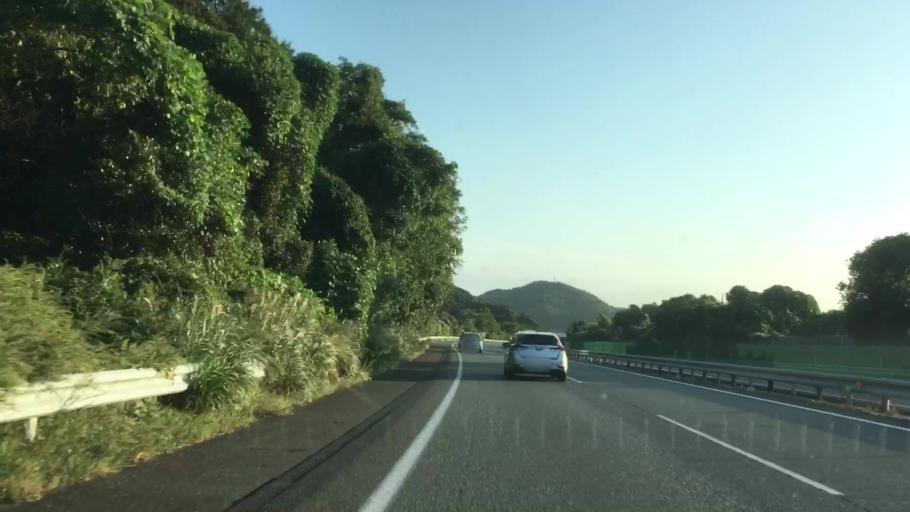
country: JP
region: Yamaguchi
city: Shimonoseki
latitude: 34.0187
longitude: 130.9579
